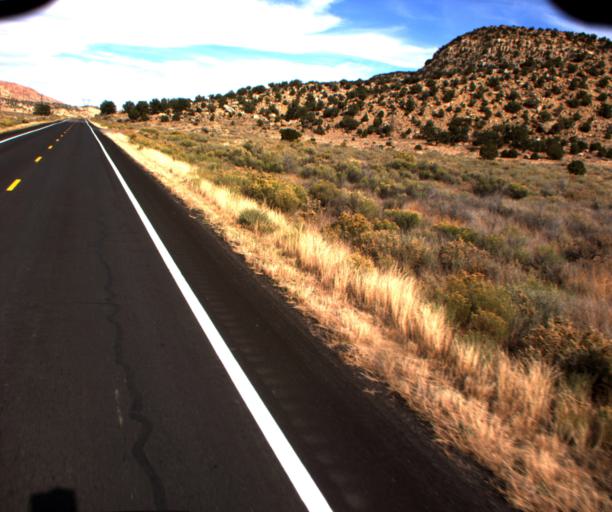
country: US
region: Arizona
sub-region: Navajo County
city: Kayenta
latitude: 36.6167
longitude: -110.4679
